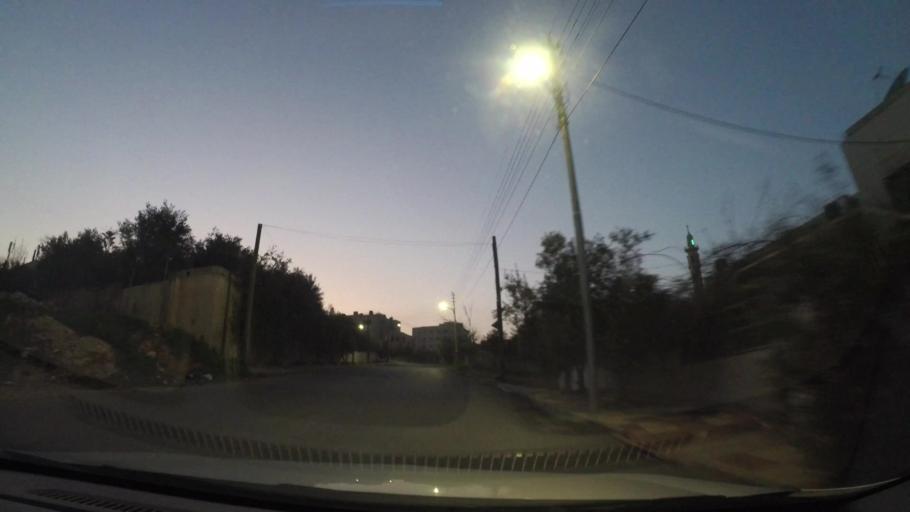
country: JO
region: Amman
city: Al Quwaysimah
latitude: 31.8924
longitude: 35.9277
